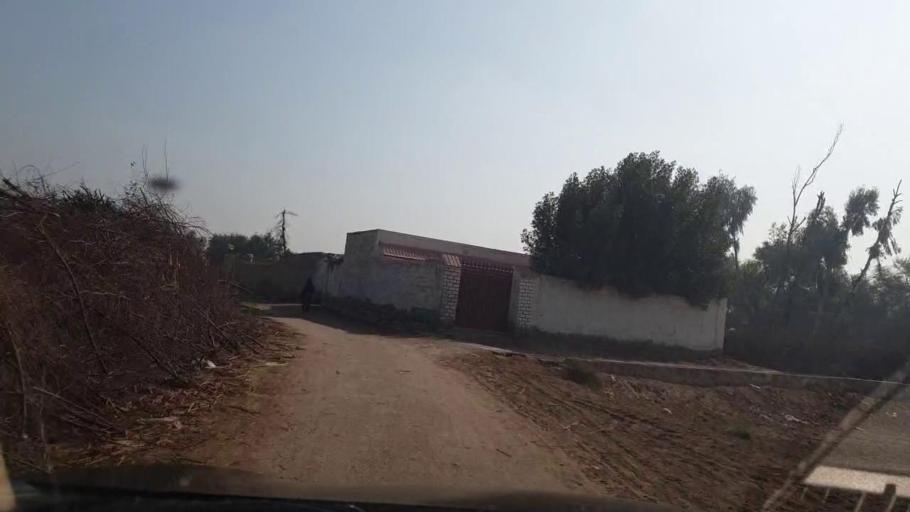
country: PK
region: Sindh
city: Ubauro
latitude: 28.1128
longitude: 69.7385
